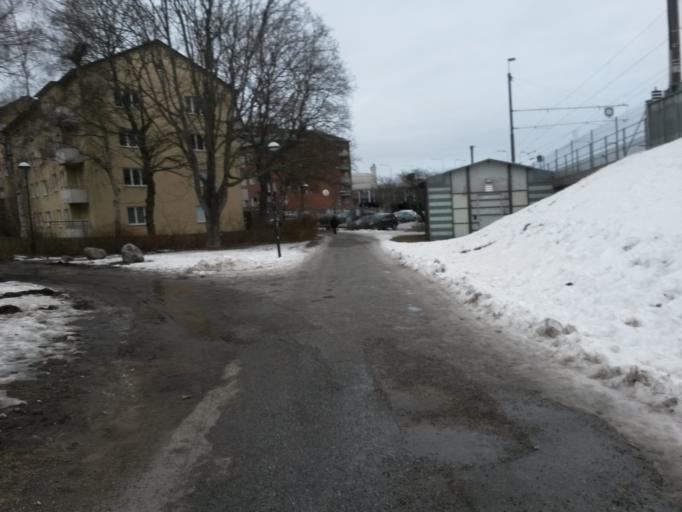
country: SE
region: Stockholm
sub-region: Stockholms Kommun
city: Arsta
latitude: 59.2969
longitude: 18.0796
